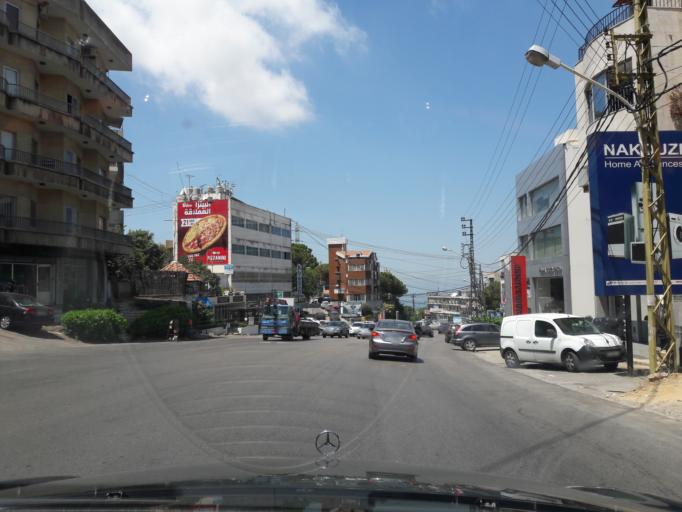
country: LB
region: Mont-Liban
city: Djounie
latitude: 33.9265
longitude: 35.6287
